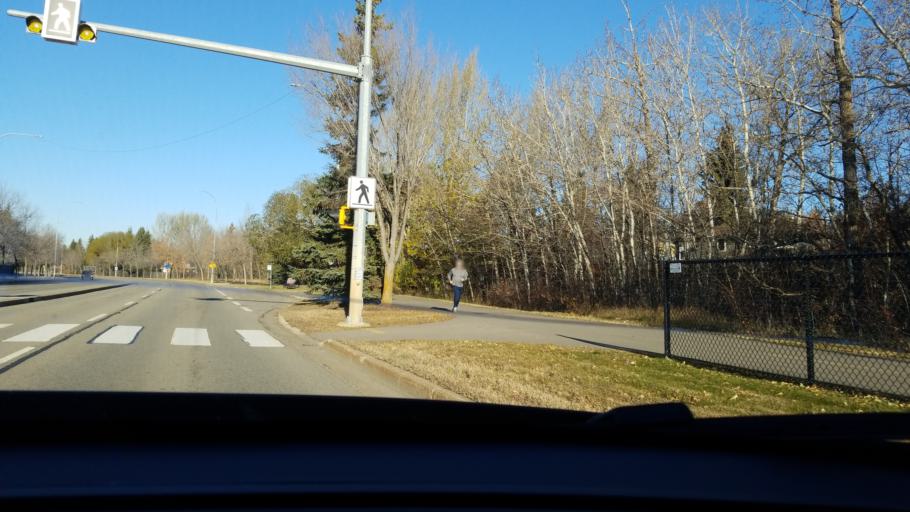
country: CA
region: Alberta
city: Sherwood Park
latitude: 53.5273
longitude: -113.2777
